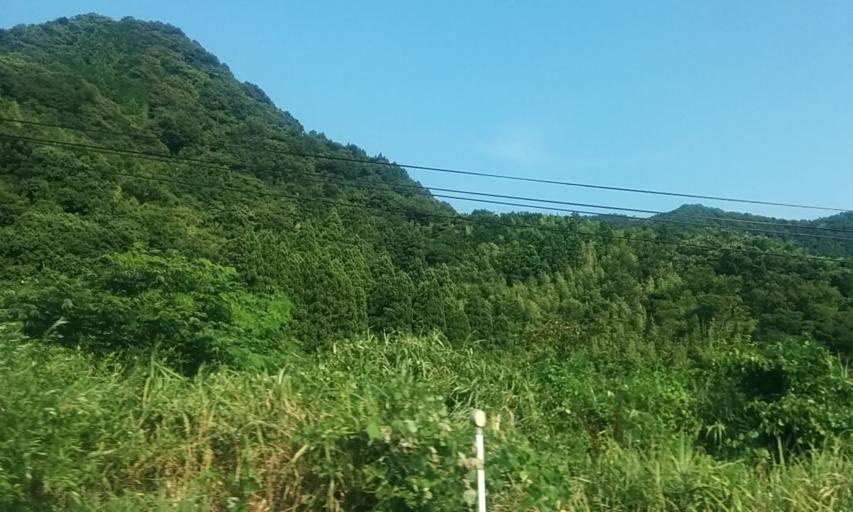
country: JP
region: Kyoto
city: Maizuru
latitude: 35.4875
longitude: 135.2850
